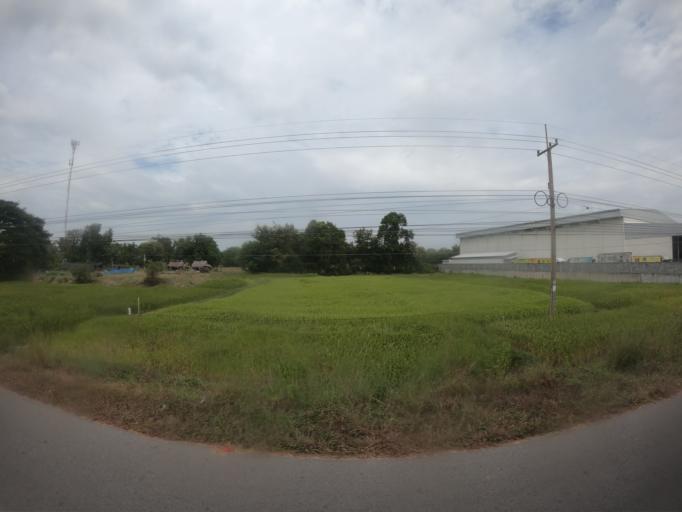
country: TH
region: Roi Et
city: Changhan
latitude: 16.0957
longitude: 103.5379
